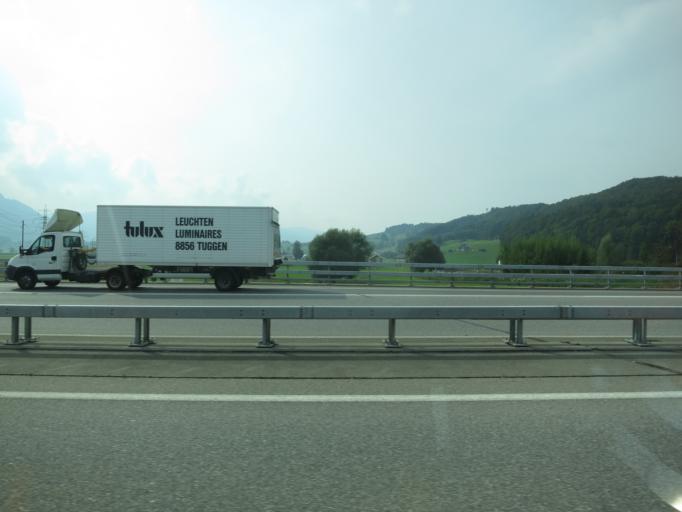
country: CH
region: Schwyz
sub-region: Bezirk March
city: Tuggen
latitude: 47.2089
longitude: 8.9630
